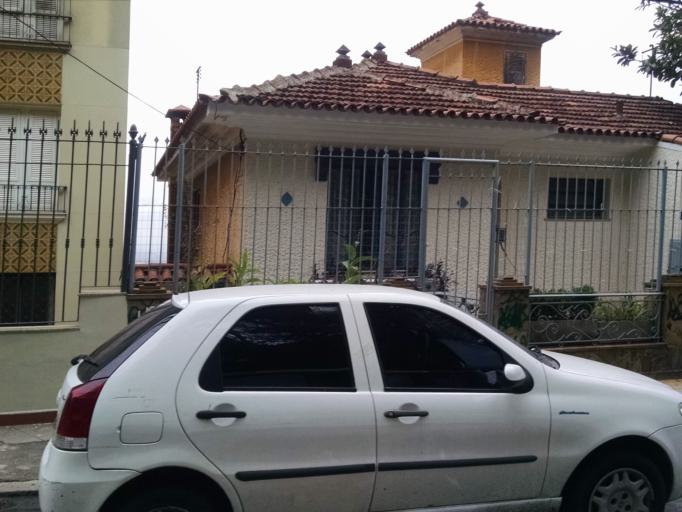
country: BR
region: Rio de Janeiro
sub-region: Rio De Janeiro
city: Rio de Janeiro
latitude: -22.9262
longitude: -43.1913
